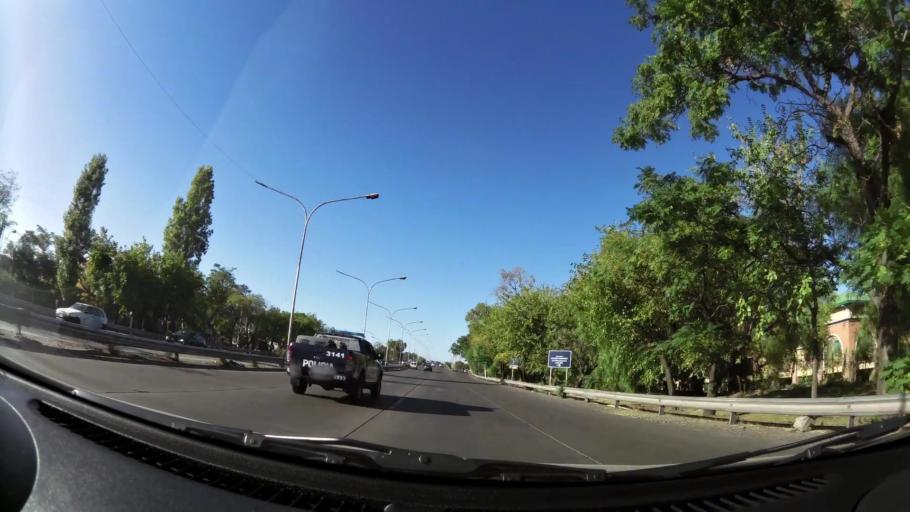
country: AR
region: Mendoza
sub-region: Departamento de Godoy Cruz
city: Godoy Cruz
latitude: -32.9158
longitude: -68.8374
